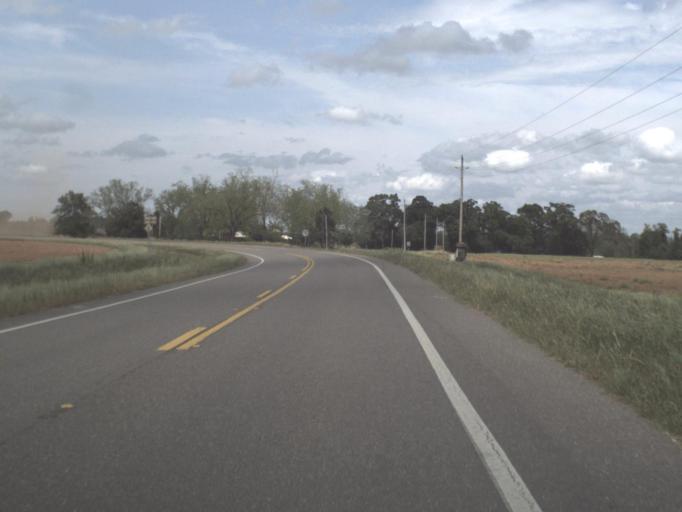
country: US
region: Alabama
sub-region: Escambia County
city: East Brewton
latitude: 30.9870
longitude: -87.1147
